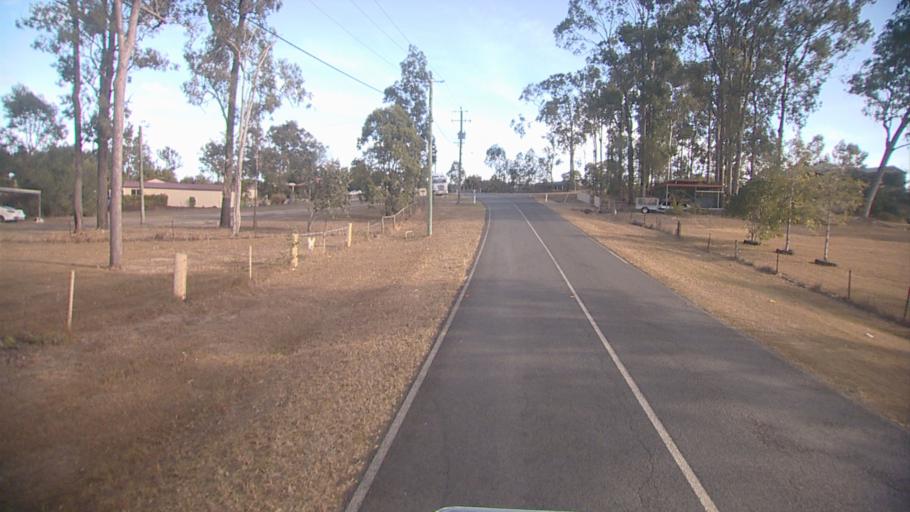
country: AU
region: Queensland
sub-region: Logan
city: Cedar Vale
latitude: -27.8670
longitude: 153.0046
